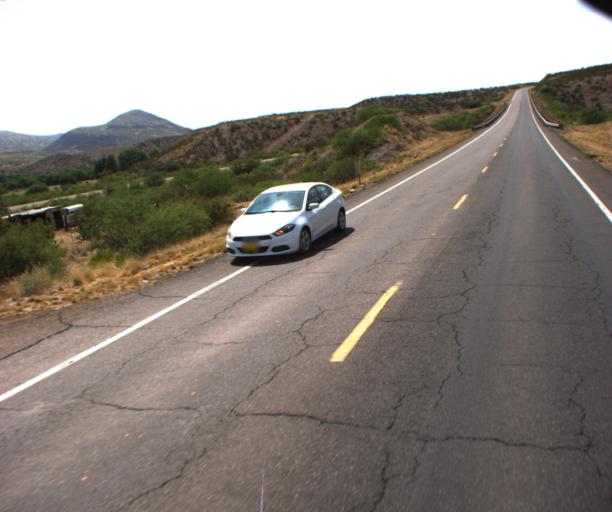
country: US
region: Arizona
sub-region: Greenlee County
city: Clifton
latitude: 32.9408
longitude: -109.2223
